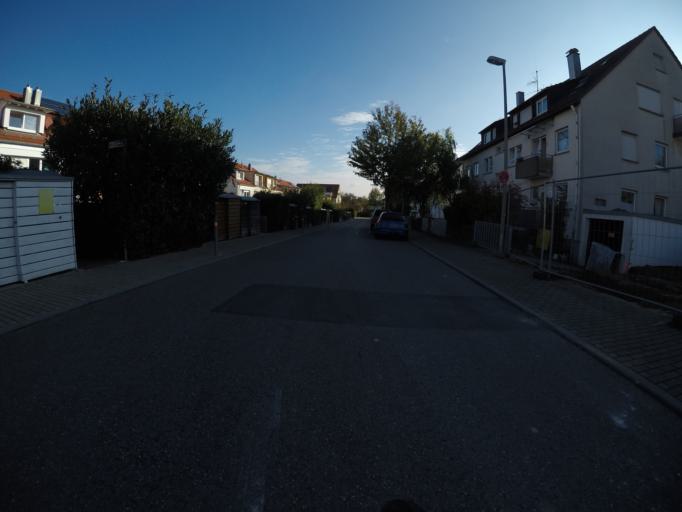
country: DE
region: Baden-Wuerttemberg
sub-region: Regierungsbezirk Stuttgart
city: Steinenbronn
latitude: 48.7362
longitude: 9.1123
